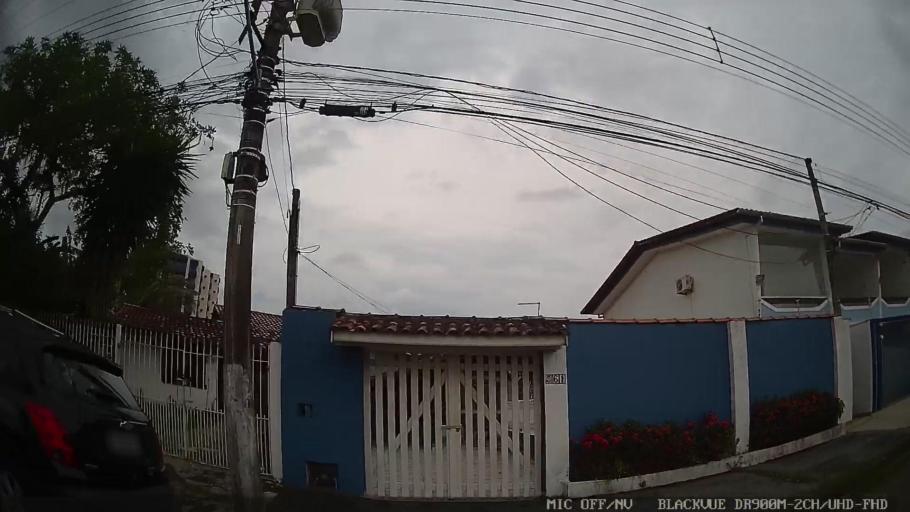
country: BR
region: Sao Paulo
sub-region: Caraguatatuba
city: Caraguatatuba
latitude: -23.6265
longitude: -45.3884
